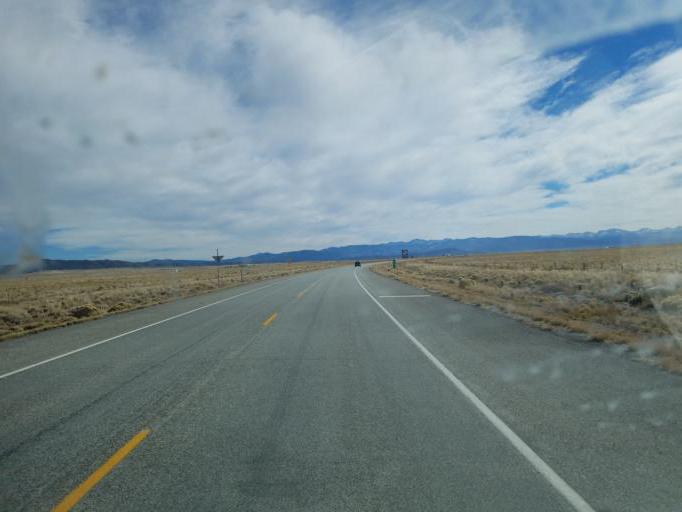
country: US
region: Colorado
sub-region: Alamosa County
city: Alamosa East
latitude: 37.4736
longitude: -105.5843
